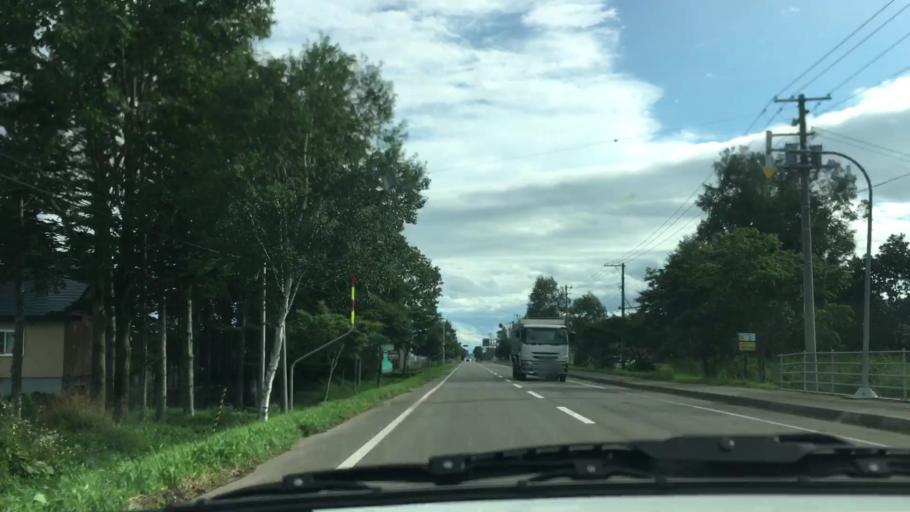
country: JP
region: Hokkaido
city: Otofuke
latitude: 43.2429
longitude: 143.2974
